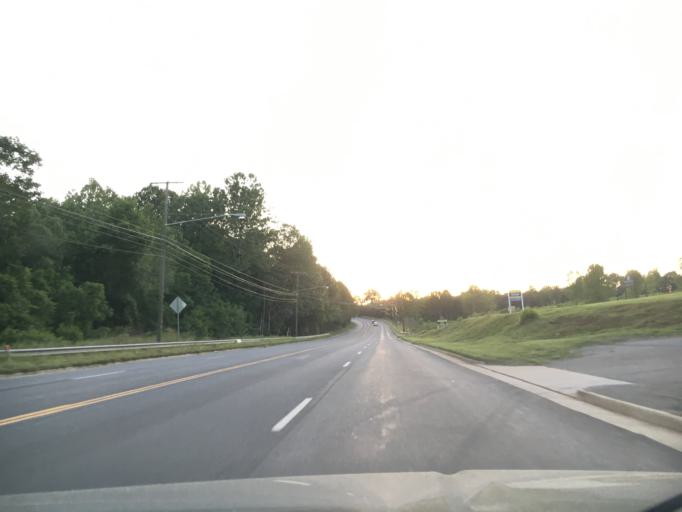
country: US
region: Virginia
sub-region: City of Lynchburg
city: West Lynchburg
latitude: 37.3753
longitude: -79.2299
